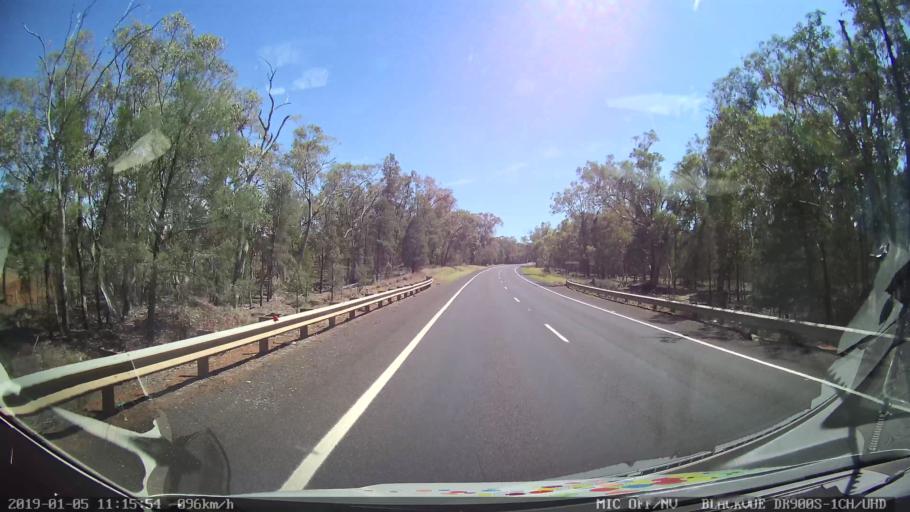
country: AU
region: New South Wales
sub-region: Warrumbungle Shire
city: Coonabarabran
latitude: -31.3464
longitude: 149.2962
